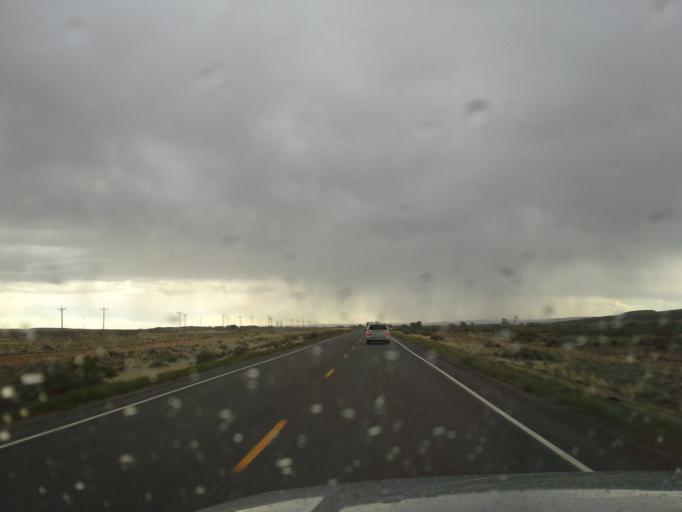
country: US
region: Wyoming
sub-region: Park County
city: Powell
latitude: 45.0201
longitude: -108.6299
